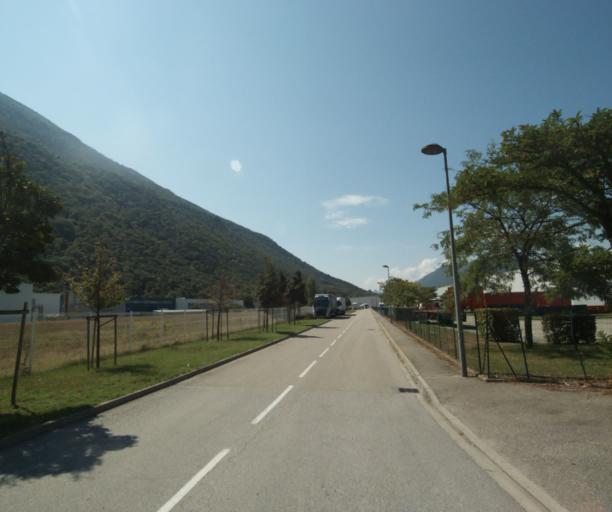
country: FR
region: Rhone-Alpes
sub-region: Departement de l'Isere
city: Champ-sur-Drac
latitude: 45.0682
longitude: 5.7234
